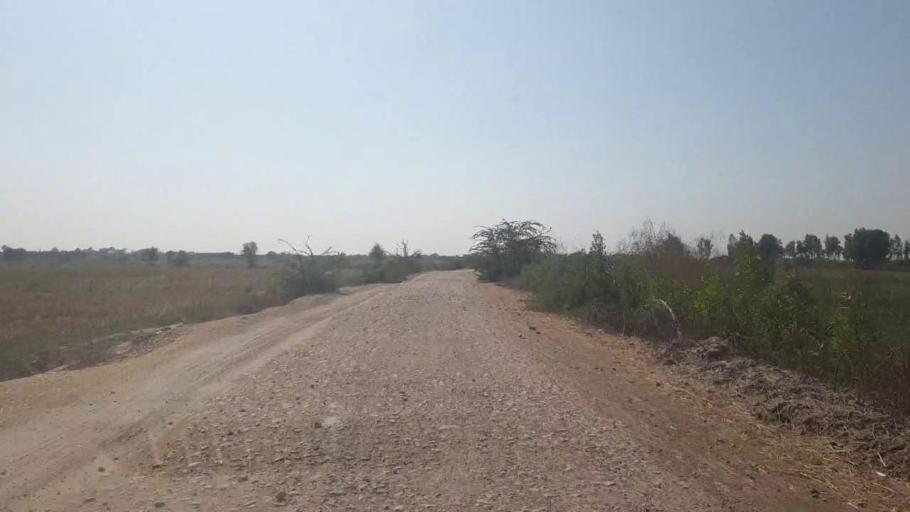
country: PK
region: Sindh
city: Badin
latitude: 24.5959
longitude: 68.8539
